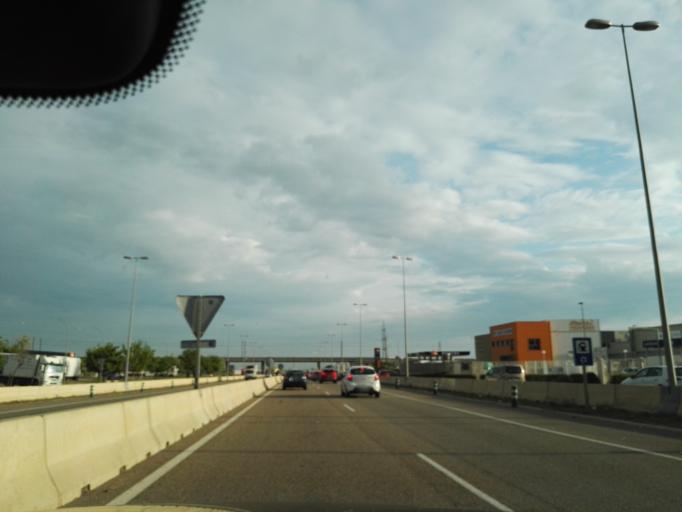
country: ES
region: Aragon
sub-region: Provincia de Zaragoza
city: Montecanal
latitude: 41.6350
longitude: -0.9898
